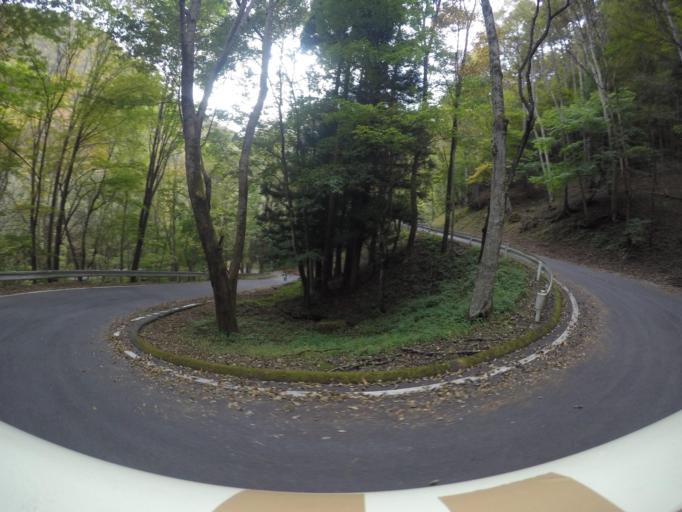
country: JP
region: Nagano
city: Saku
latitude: 36.0684
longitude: 138.6583
